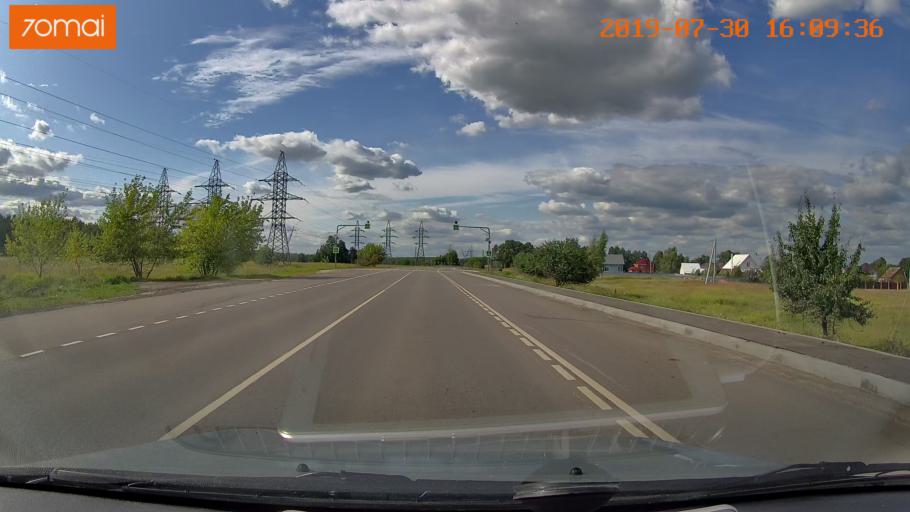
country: RU
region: Moskovskaya
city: Peski
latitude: 55.2545
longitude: 38.7177
